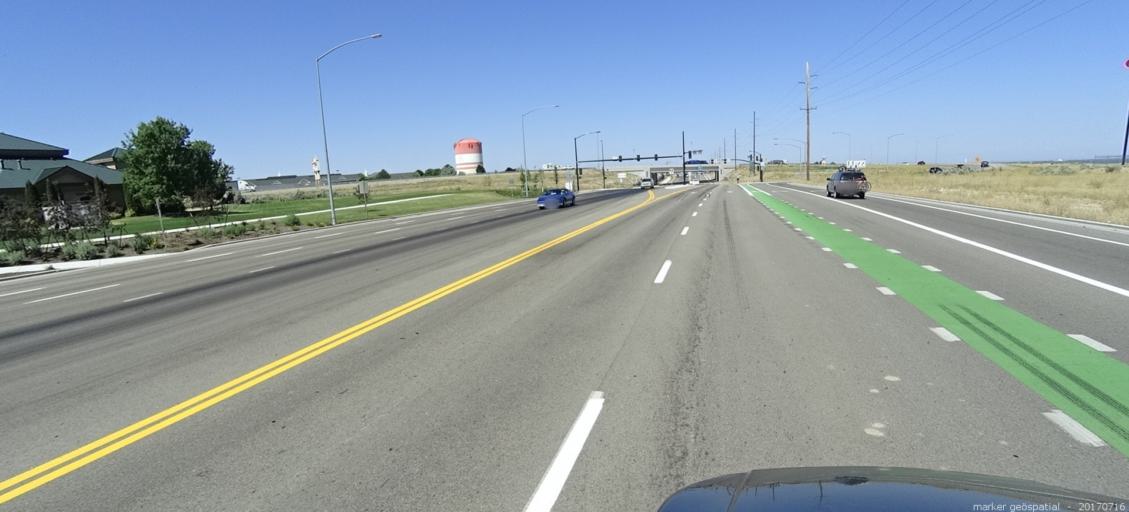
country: US
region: Idaho
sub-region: Ada County
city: Boise
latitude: 43.5414
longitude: -116.1573
